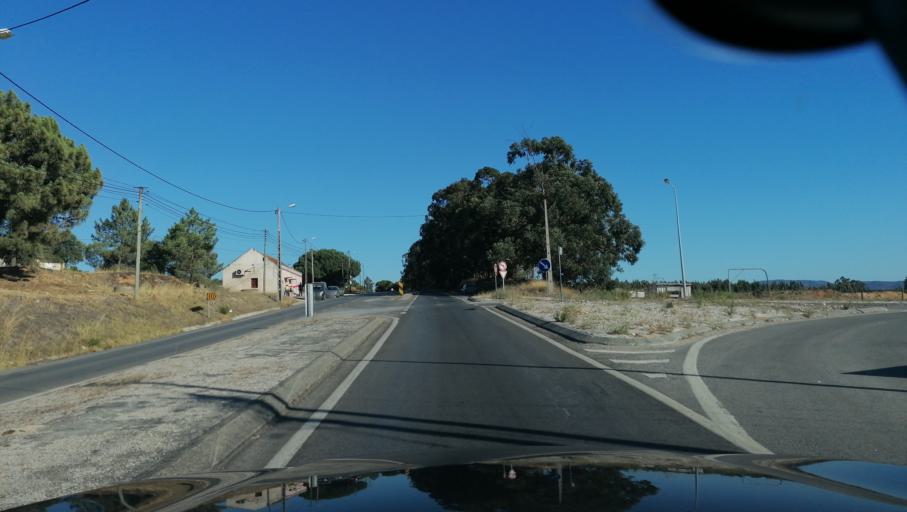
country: PT
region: Setubal
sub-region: Moita
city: Moita
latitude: 38.6325
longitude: -8.9692
